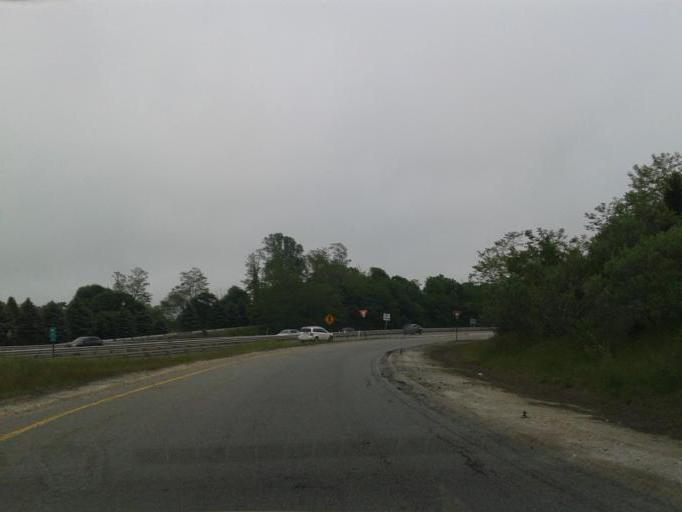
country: US
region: Massachusetts
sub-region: Plymouth County
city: Plymouth
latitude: 41.9524
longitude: -70.6814
